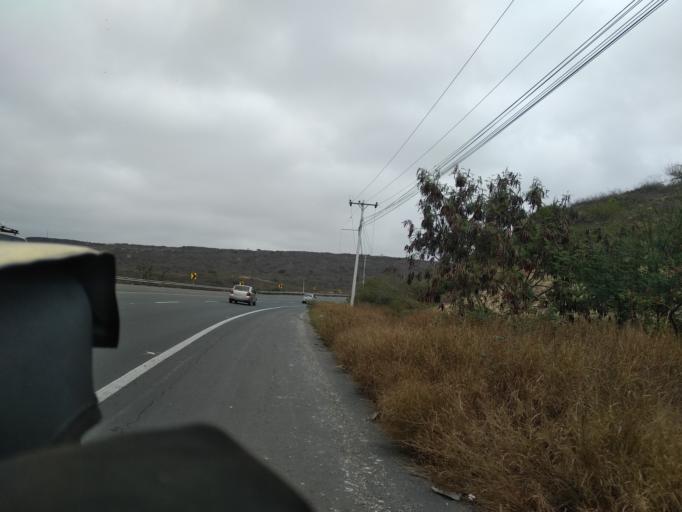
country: EC
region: Santa Elena
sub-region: Canton Santa Elena
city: Santa Elena
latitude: -2.2035
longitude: -80.8541
